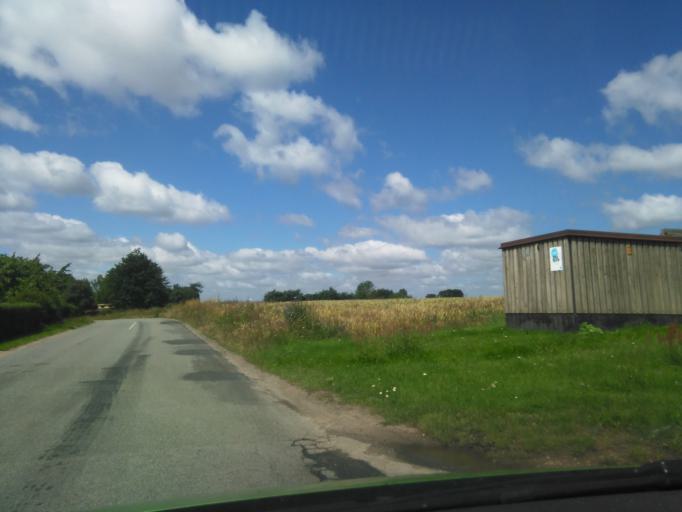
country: DK
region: Central Jutland
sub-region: Syddjurs Kommune
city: Ronde
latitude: 56.1969
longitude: 10.4333
